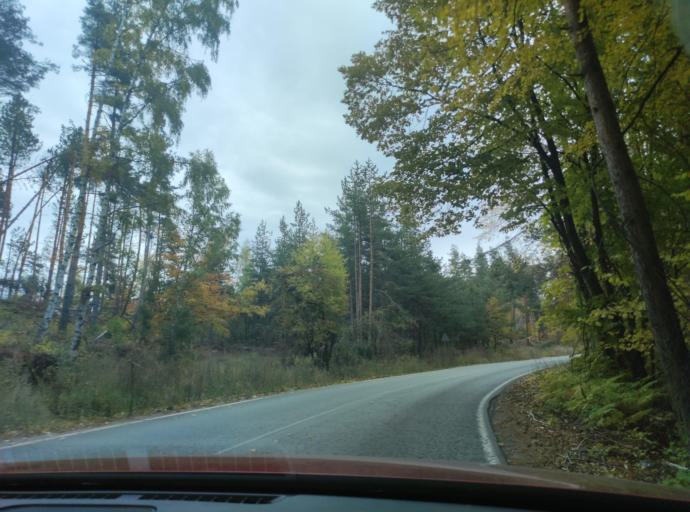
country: BG
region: Sofiya
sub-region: Obshtina Godech
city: Godech
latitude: 43.0177
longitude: 23.1208
